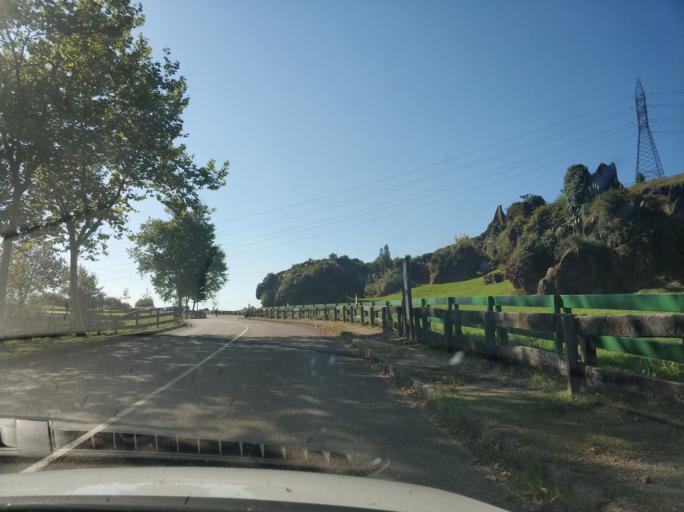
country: ES
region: Cantabria
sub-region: Provincia de Cantabria
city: Penagos
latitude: 43.3516
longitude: -3.8434
